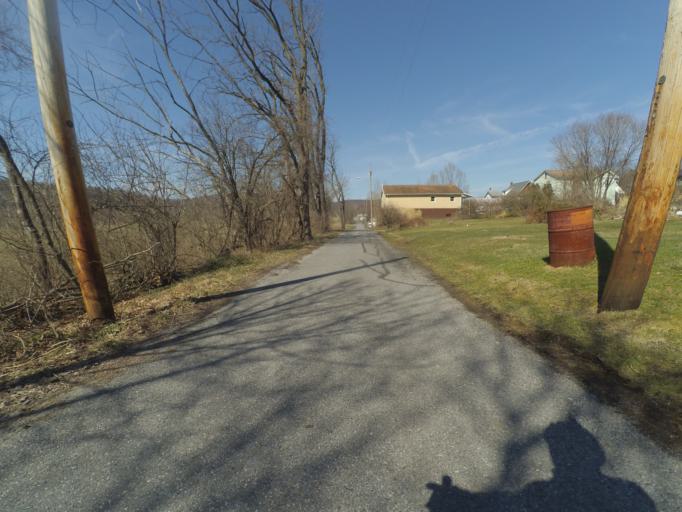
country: US
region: Pennsylvania
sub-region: Centre County
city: Milesburg
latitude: 40.9364
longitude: -77.7862
